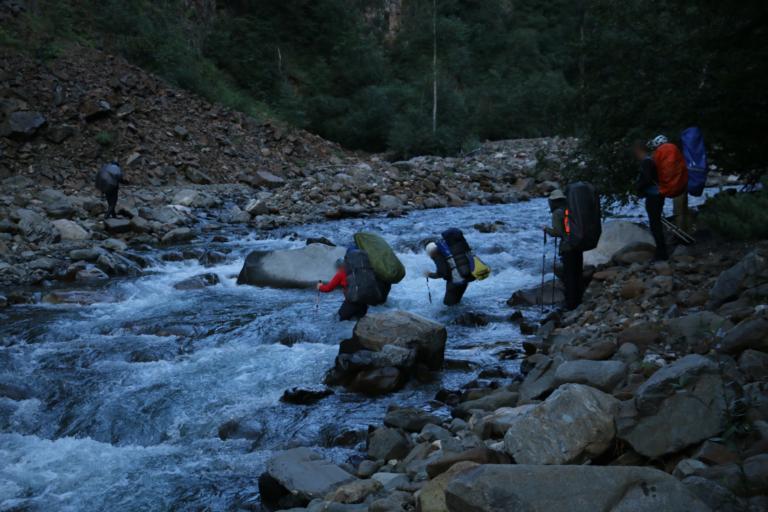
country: RU
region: Respublika Buryatiya
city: Novyy Uoyan
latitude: 56.3003
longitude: 111.3558
